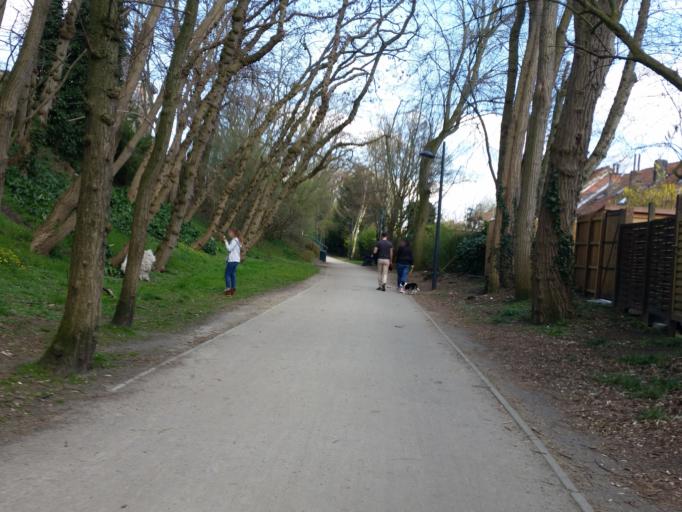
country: BE
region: Flanders
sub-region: Provincie Vlaams-Brabant
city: Kraainem
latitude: 50.8156
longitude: 4.4218
